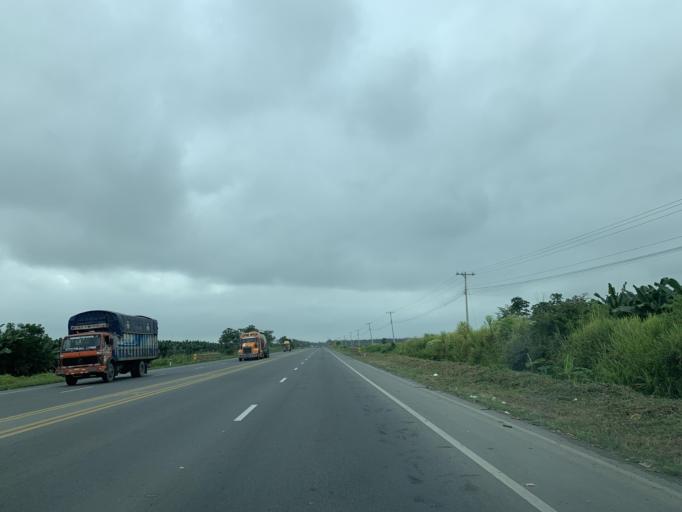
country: EC
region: Guayas
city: Coronel Marcelino Mariduena
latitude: -2.2954
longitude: -79.4983
